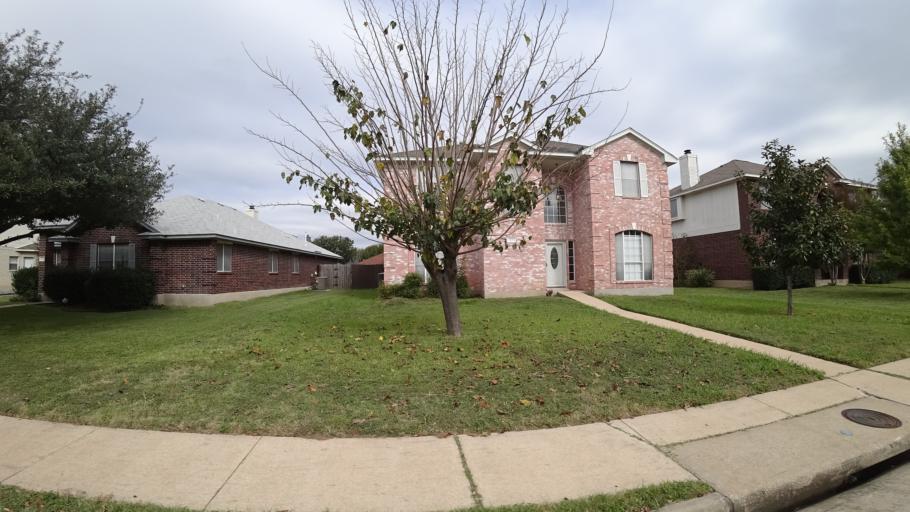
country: US
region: Texas
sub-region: Travis County
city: Windemere
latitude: 30.4621
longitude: -97.6434
